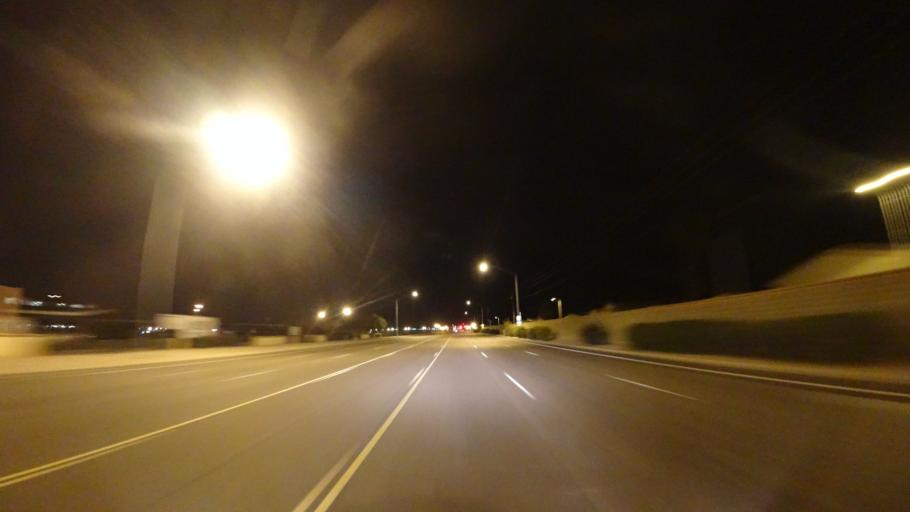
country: US
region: Arizona
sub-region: Maricopa County
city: Mesa
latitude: 33.4618
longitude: -111.7187
